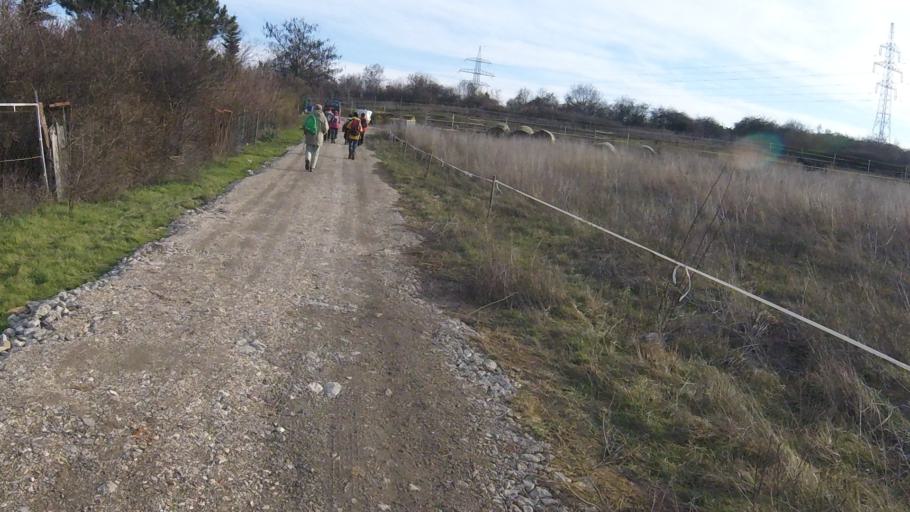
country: HU
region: Pest
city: Urom
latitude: 47.5999
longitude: 19.0304
